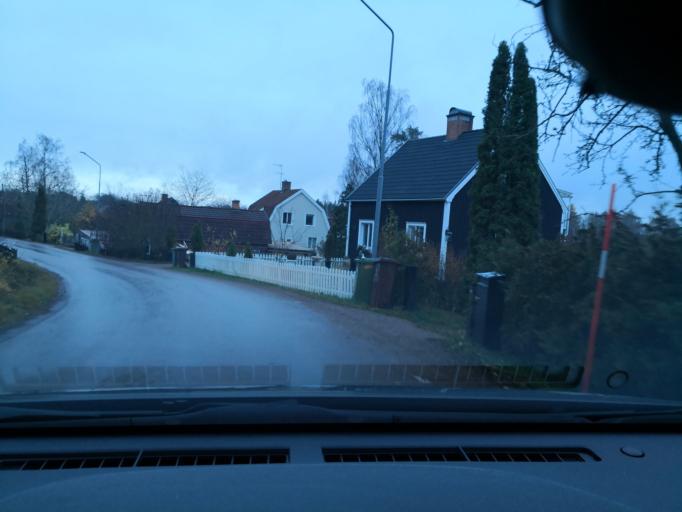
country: SE
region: Vaestmanland
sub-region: Hallstahammars Kommun
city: Kolback
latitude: 59.5593
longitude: 16.2129
